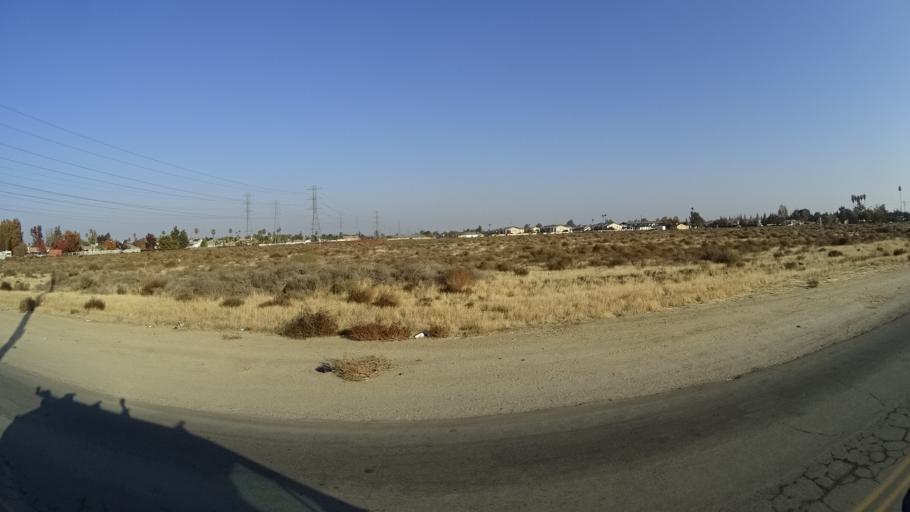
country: US
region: California
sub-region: Kern County
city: Rosedale
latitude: 35.3860
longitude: -119.1547
